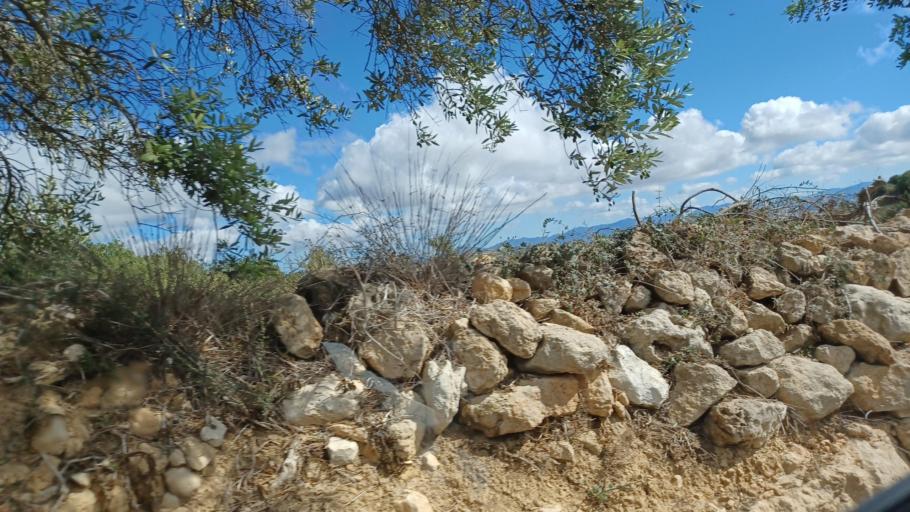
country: CY
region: Pafos
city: Tala
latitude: 34.8571
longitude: 32.4478
